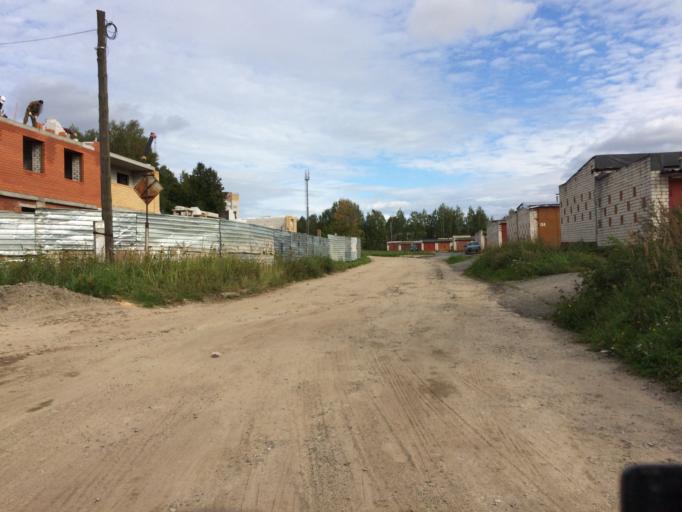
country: RU
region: Mariy-El
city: Yoshkar-Ola
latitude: 56.6509
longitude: 47.9614
